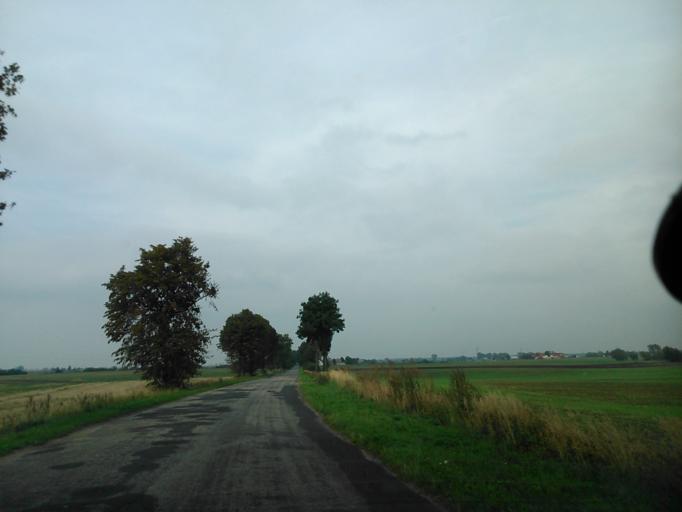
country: PL
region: Kujawsko-Pomorskie
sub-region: Powiat wabrzeski
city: Pluznica
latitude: 53.2433
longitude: 18.8197
